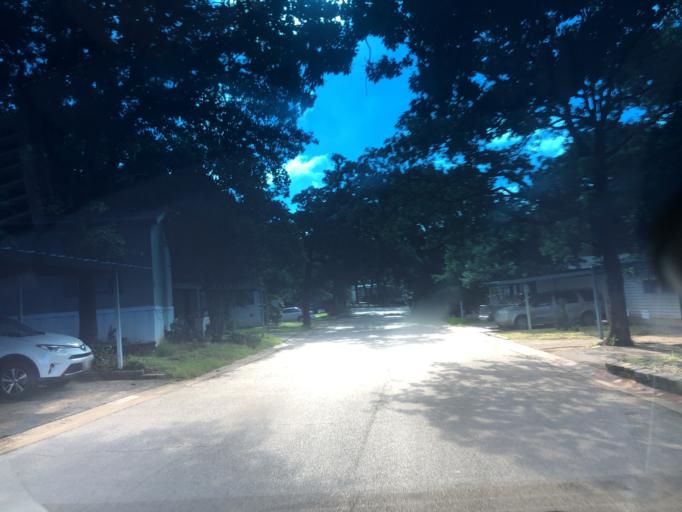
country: US
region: Texas
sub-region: Dallas County
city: Irving
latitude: 32.8094
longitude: -96.9998
